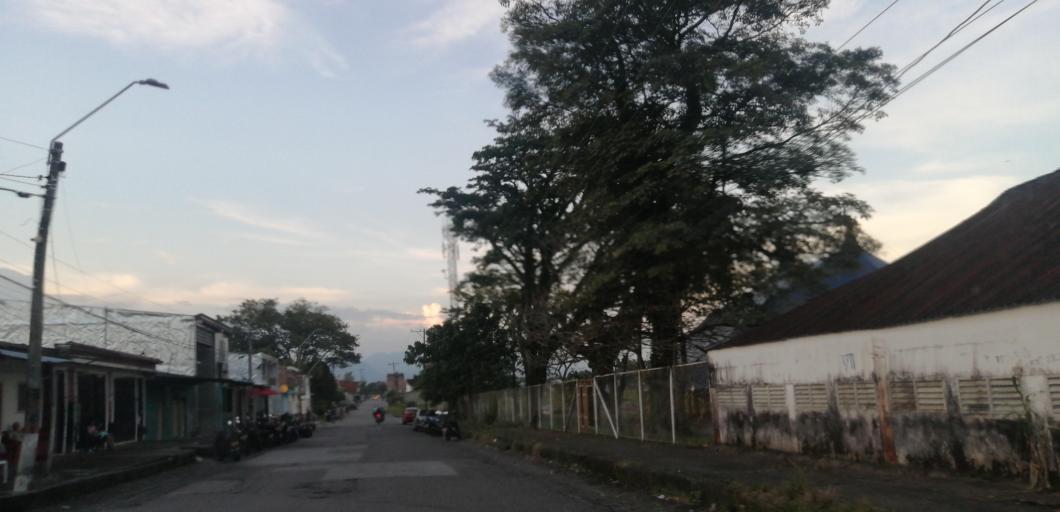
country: CO
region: Meta
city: Acacias
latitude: 3.9914
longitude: -73.7570
